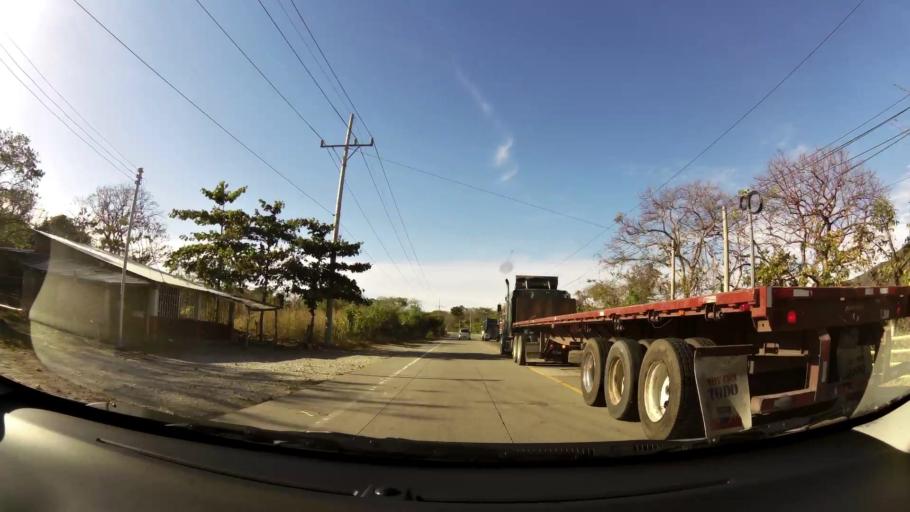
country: SV
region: Santa Ana
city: Metapan
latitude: 14.2348
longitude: -89.4680
